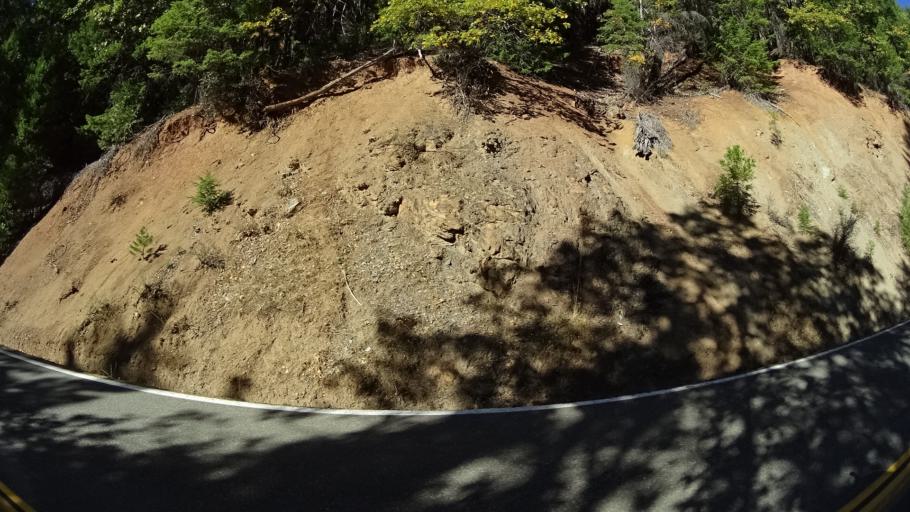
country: US
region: California
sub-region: Trinity County
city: Weaverville
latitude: 41.2153
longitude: -123.0273
